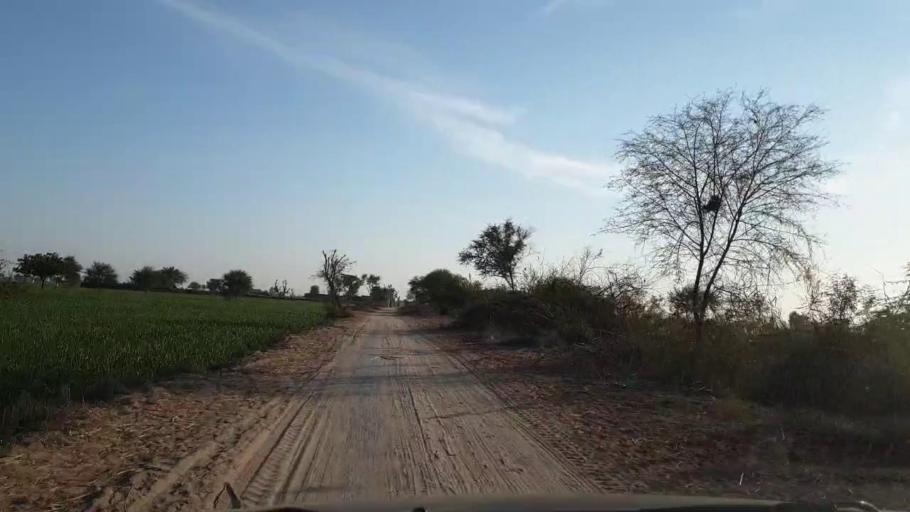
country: PK
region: Sindh
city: Khadro
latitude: 26.2231
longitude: 68.7399
